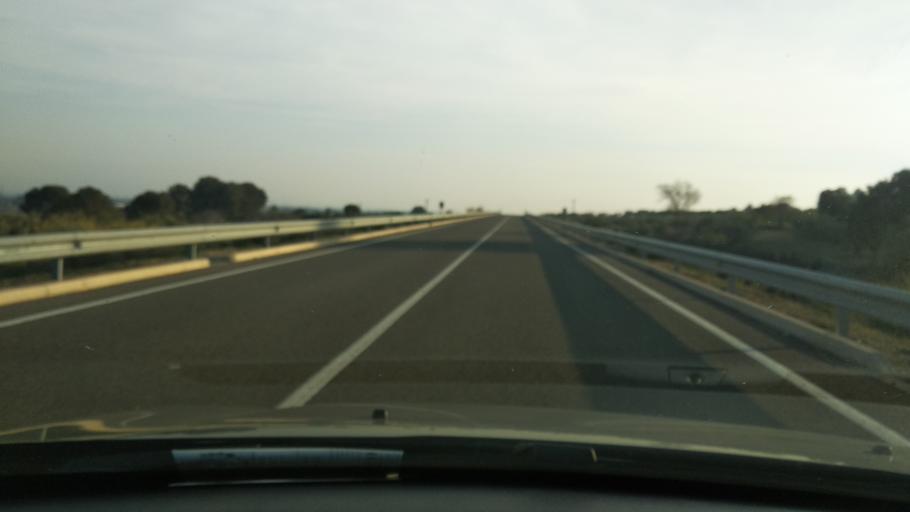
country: ES
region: Catalonia
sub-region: Provincia de Tarragona
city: les Borges del Camp
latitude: 41.1740
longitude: 1.0094
